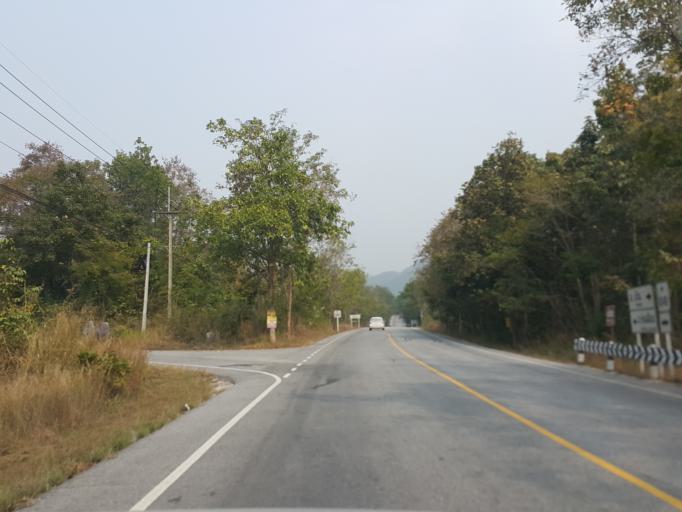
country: TH
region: Lampang
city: Thoen
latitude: 17.6413
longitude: 99.2842
